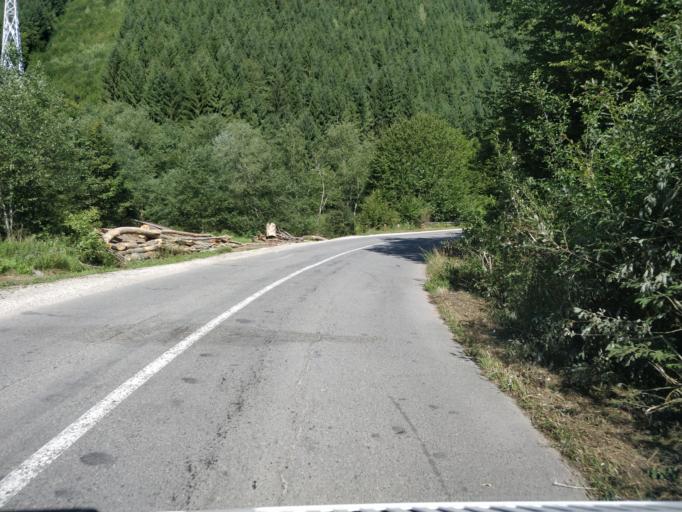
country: RO
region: Cluj
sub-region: Comuna Sacueu
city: Sacuieu
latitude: 46.8353
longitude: 22.8600
